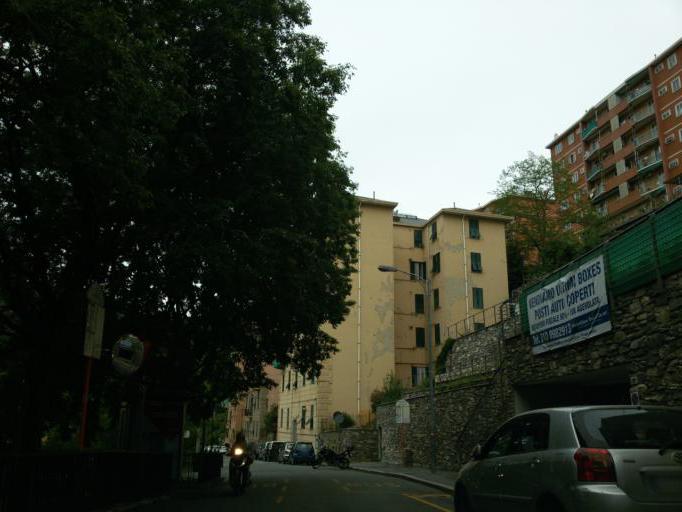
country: IT
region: Liguria
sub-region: Provincia di Genova
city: Genoa
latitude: 44.4264
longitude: 8.9249
